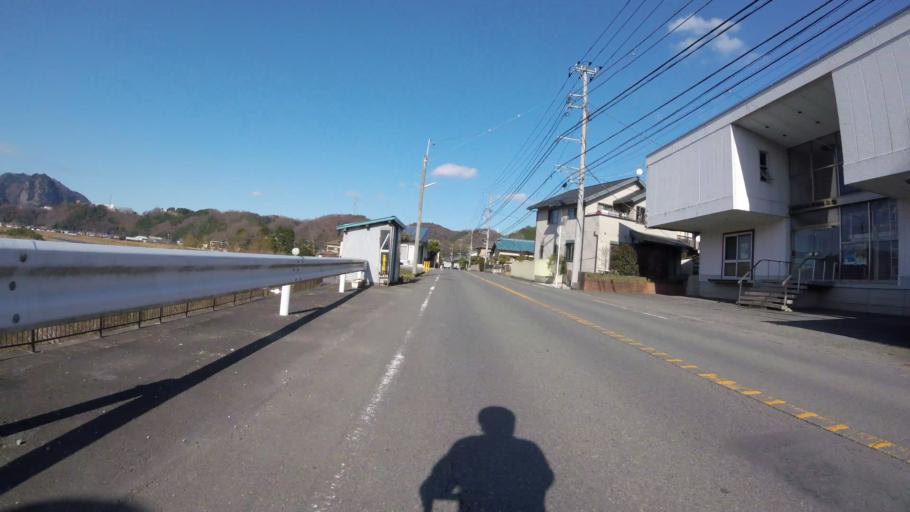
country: JP
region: Shizuoka
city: Ito
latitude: 34.9868
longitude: 138.9534
